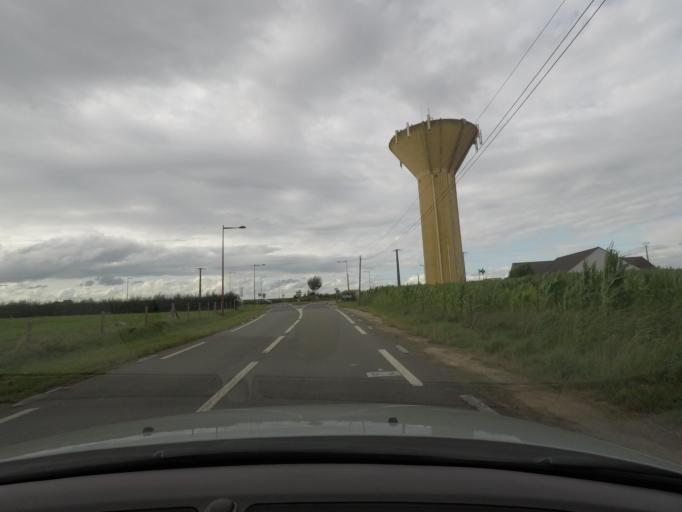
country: FR
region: Haute-Normandie
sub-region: Departement de la Seine-Maritime
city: Ymare
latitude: 49.3552
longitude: 1.1828
